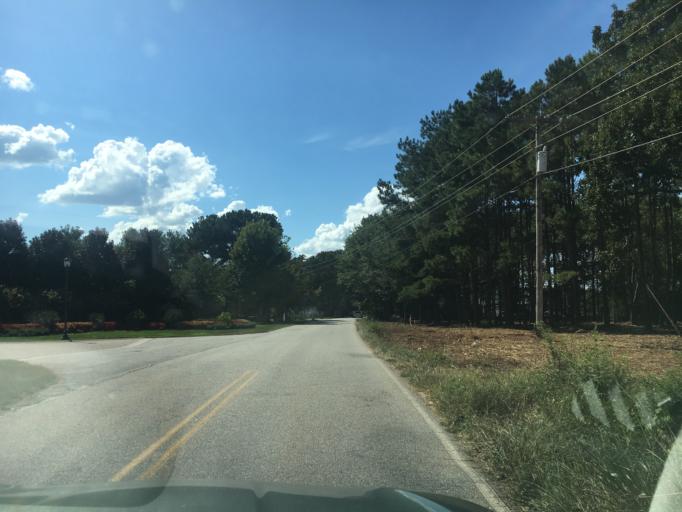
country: US
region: South Carolina
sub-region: Greenville County
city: Five Forks
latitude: 34.8189
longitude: -82.2169
